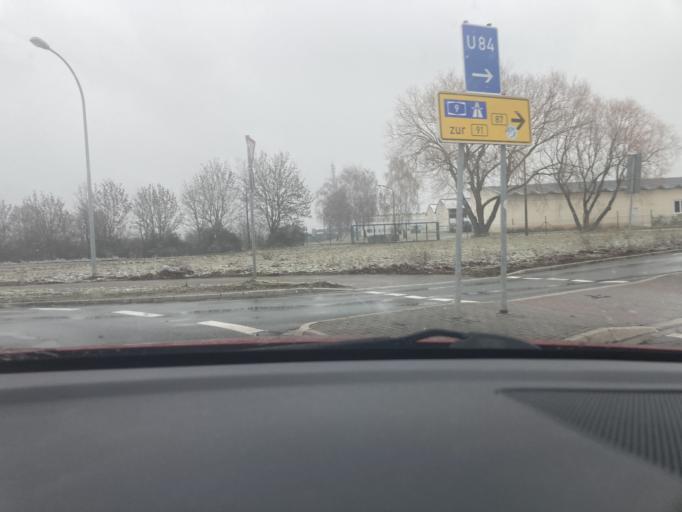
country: DE
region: Saxony-Anhalt
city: Weissenfels
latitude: 51.1884
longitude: 11.9896
